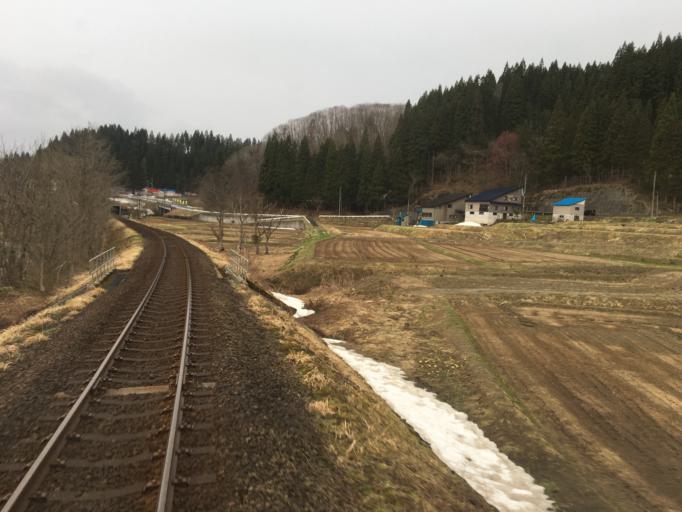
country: JP
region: Akita
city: Takanosu
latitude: 39.9202
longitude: 140.5095
